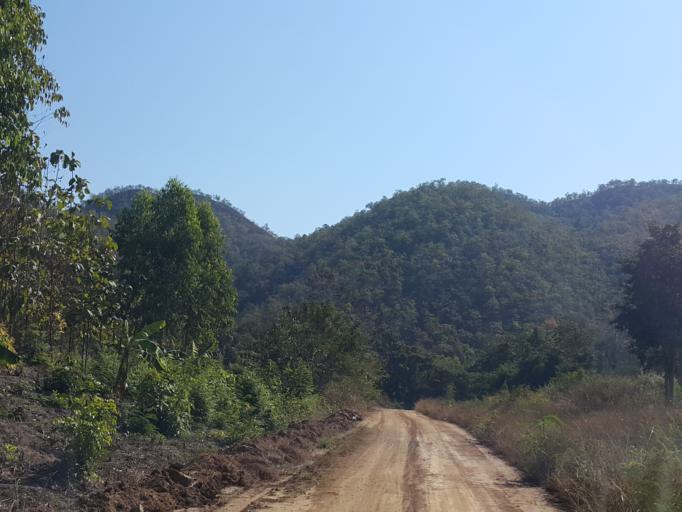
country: TH
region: Sukhothai
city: Thung Saliam
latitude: 17.3218
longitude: 99.4617
